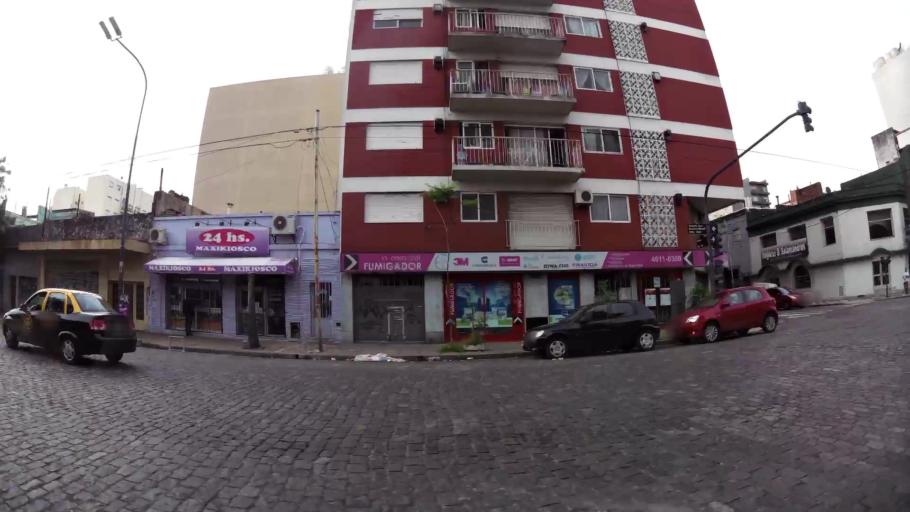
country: AR
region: Buenos Aires F.D.
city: Villa Santa Rita
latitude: -34.6338
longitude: -58.4702
